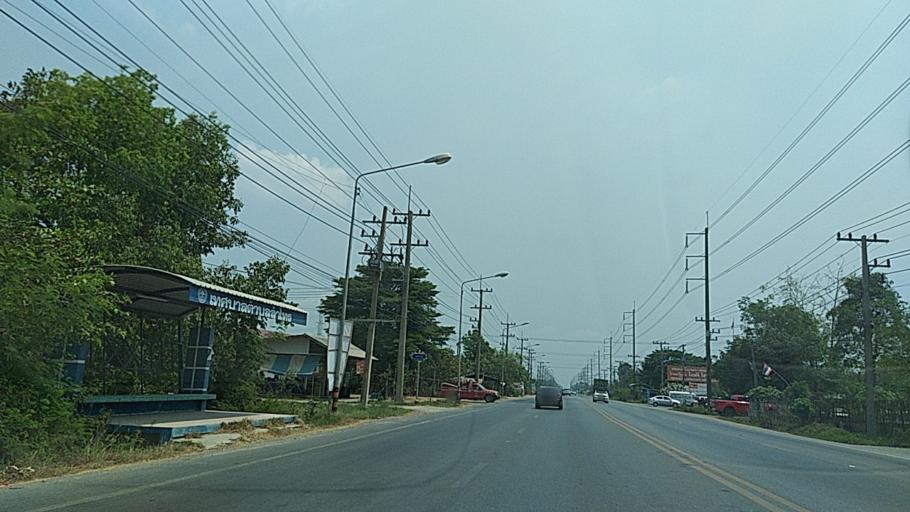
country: TH
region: Pathum Thani
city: Ban Lam Luk Ka
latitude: 13.9588
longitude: 100.8731
